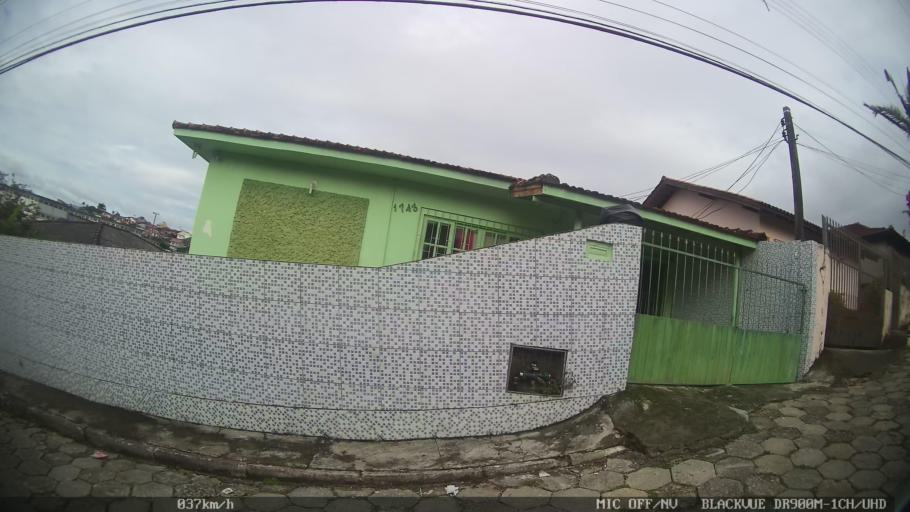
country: BR
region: Santa Catarina
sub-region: Sao Jose
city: Campinas
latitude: -27.5510
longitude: -48.6331
